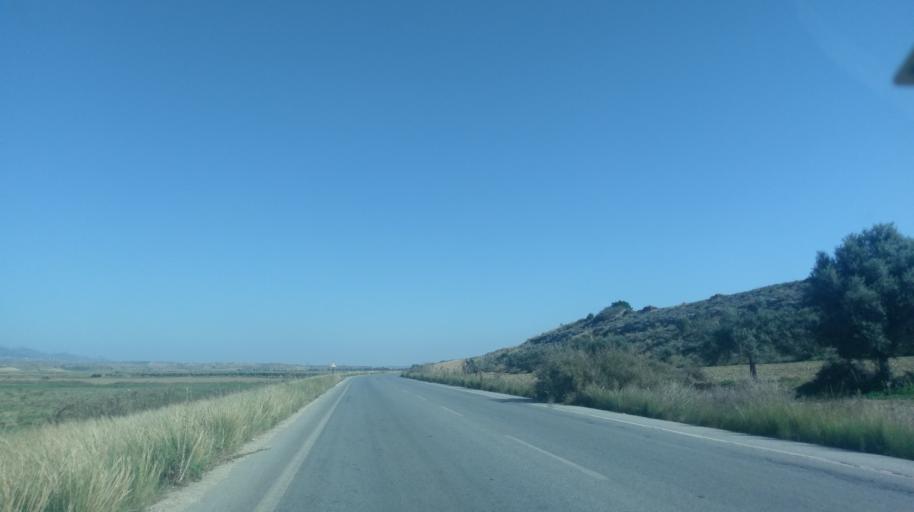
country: CY
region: Ammochostos
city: Trikomo
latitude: 35.2710
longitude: 33.8147
